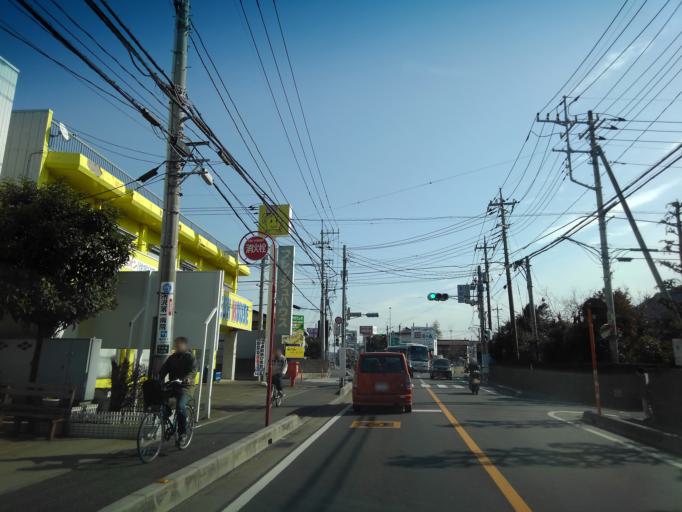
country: JP
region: Saitama
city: Tokorozawa
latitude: 35.7914
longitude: 139.4984
